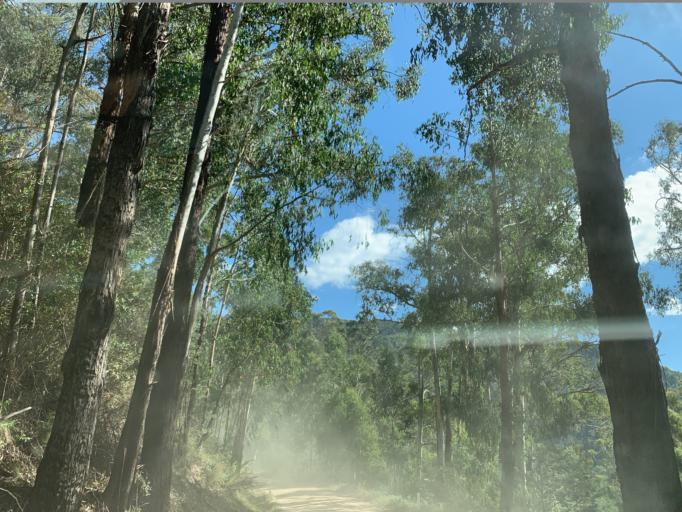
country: AU
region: Victoria
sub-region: Mansfield
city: Mansfield
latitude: -37.0979
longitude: 146.4851
